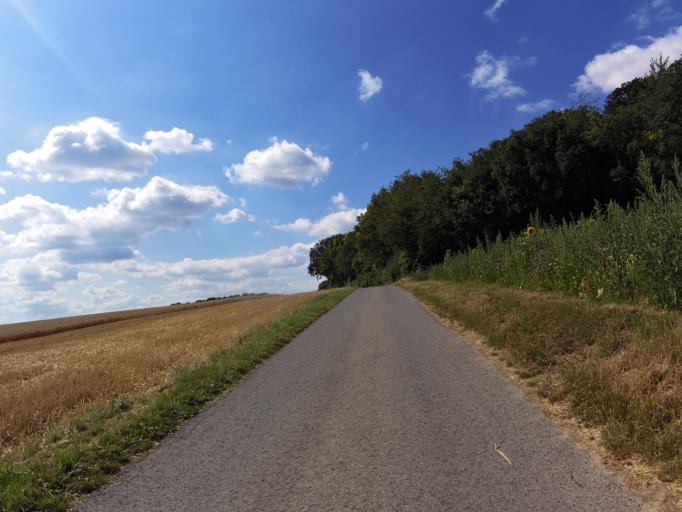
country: DE
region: Bavaria
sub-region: Regierungsbezirk Unterfranken
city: Gerbrunn
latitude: 49.7800
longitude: 10.0149
